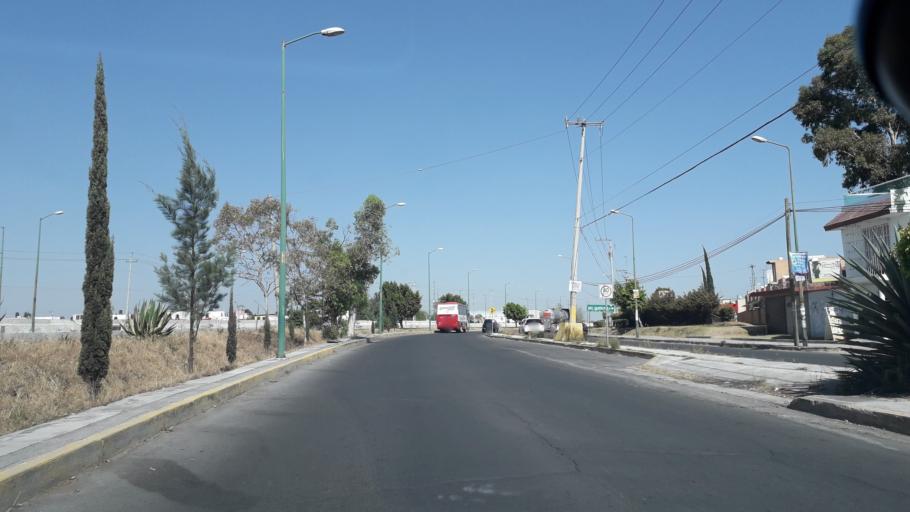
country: MX
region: Puebla
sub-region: Puebla
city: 18 de Marzo
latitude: 18.9781
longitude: -98.2161
